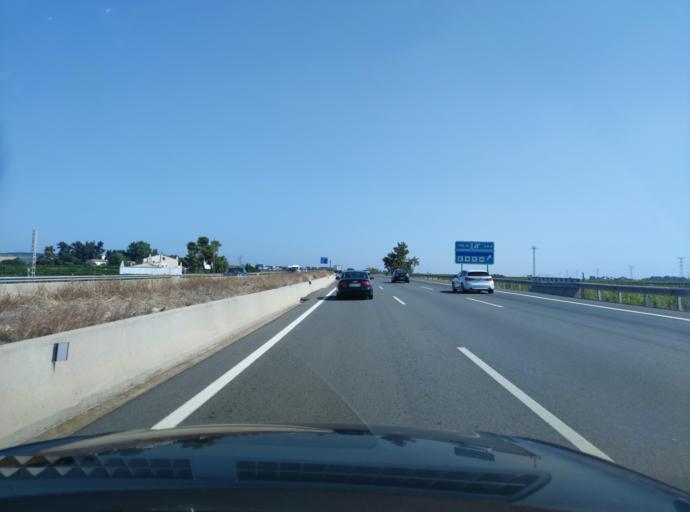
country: ES
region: Valencia
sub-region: Provincia de Valencia
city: Alginet
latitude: 39.2663
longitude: -0.4584
